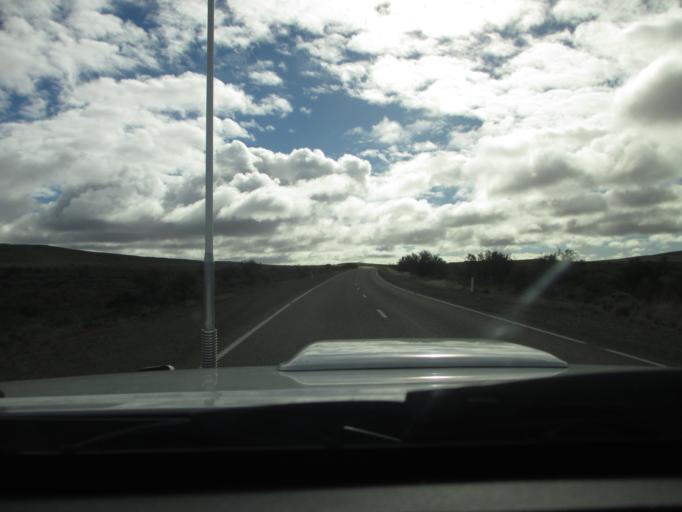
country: AU
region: South Australia
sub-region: Flinders Ranges
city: Quorn
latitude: -32.1951
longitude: 138.5329
